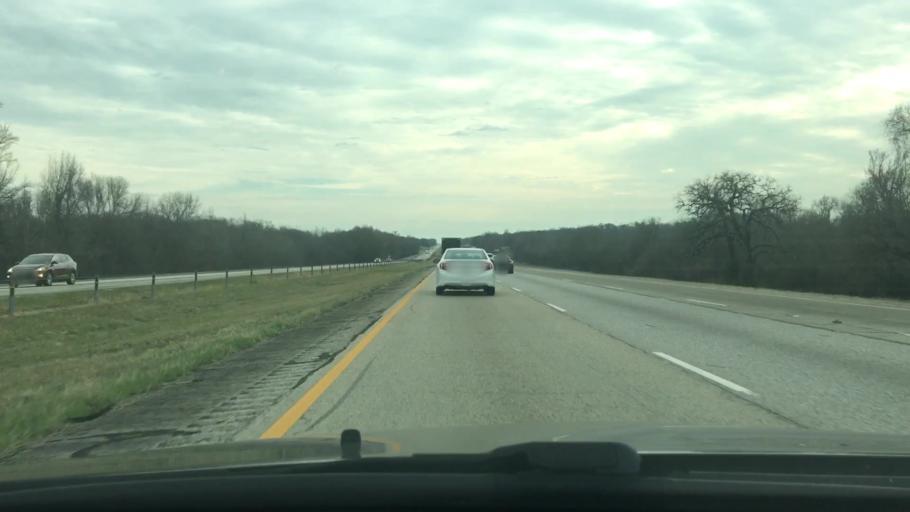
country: US
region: Texas
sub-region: Leon County
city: Centerville
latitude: 31.1922
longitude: -95.9928
